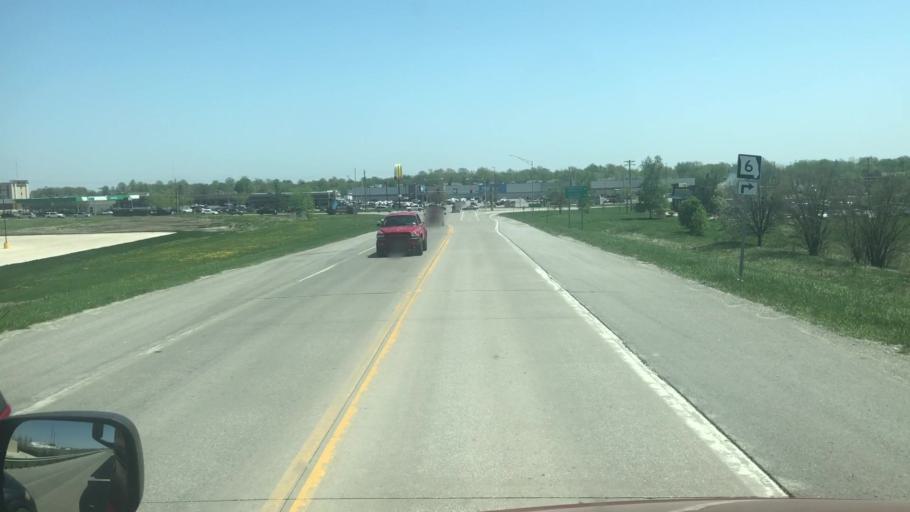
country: US
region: Missouri
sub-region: Adair County
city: Kirksville
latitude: 40.2167
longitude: -92.5855
